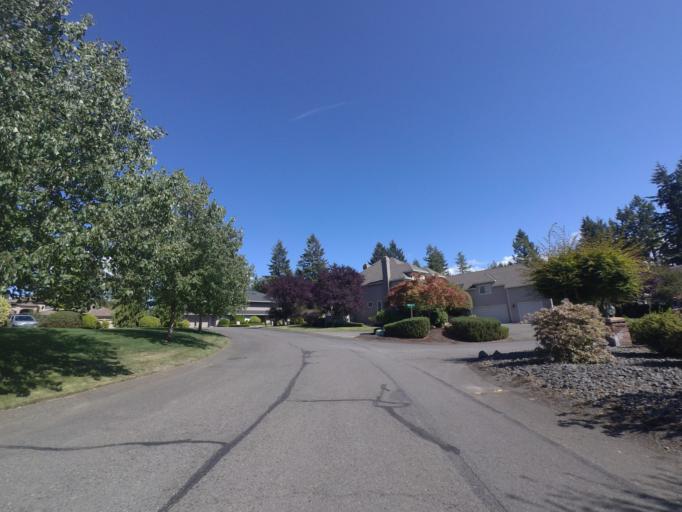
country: US
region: Washington
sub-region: Pierce County
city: Fircrest
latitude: 47.2128
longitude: -122.5181
